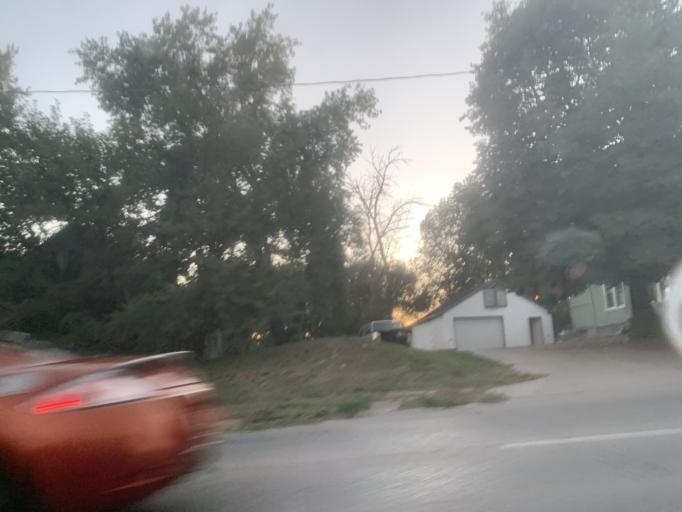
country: US
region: Nebraska
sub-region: Douglas County
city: Omaha
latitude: 41.2156
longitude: -95.9762
